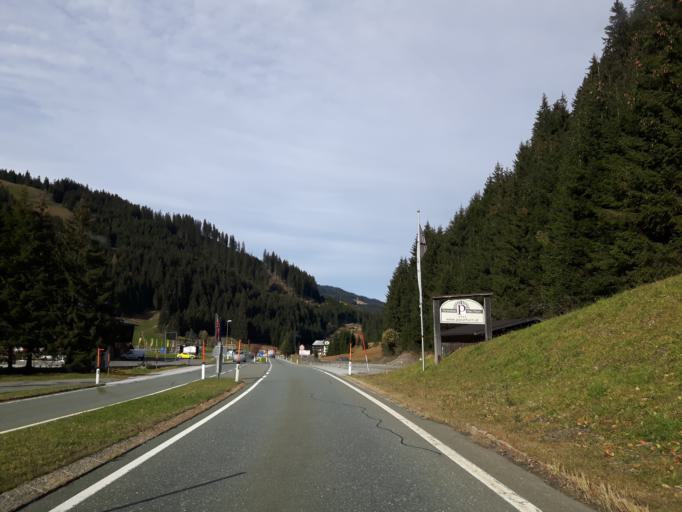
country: AT
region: Salzburg
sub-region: Politischer Bezirk Zell am See
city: Hollersbach im Pinzgau
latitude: 47.3174
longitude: 12.4094
